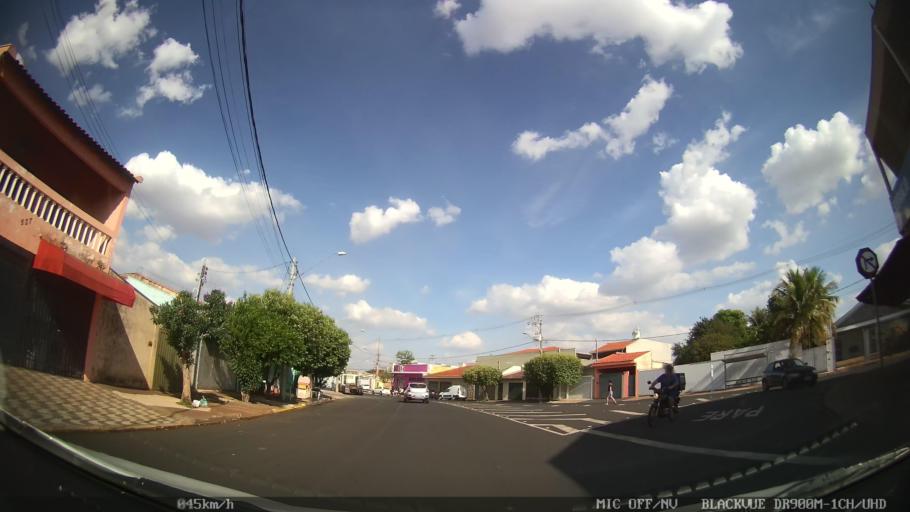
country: BR
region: Sao Paulo
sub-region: Ribeirao Preto
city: Ribeirao Preto
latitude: -21.1988
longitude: -47.8401
